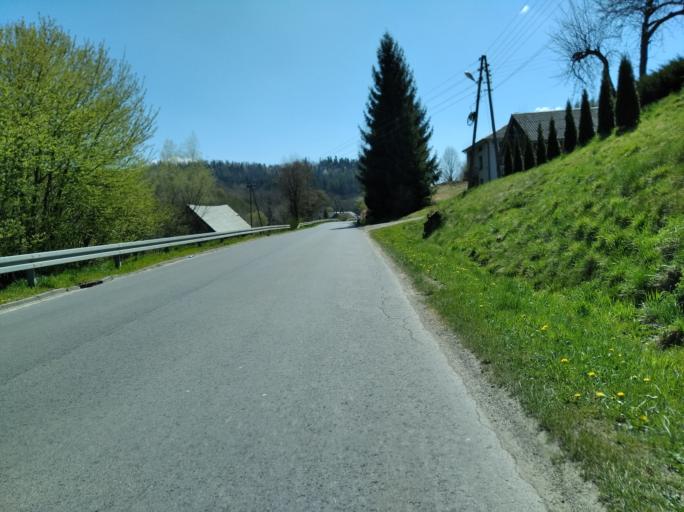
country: PL
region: Subcarpathian Voivodeship
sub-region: Powiat brzozowski
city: Dydnia
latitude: 49.6905
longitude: 22.1846
